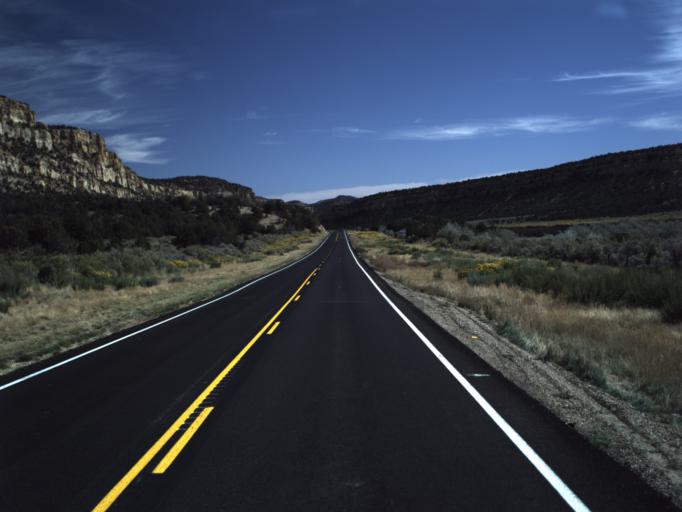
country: US
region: Utah
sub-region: Garfield County
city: Panguitch
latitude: 37.7272
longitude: -111.7710
